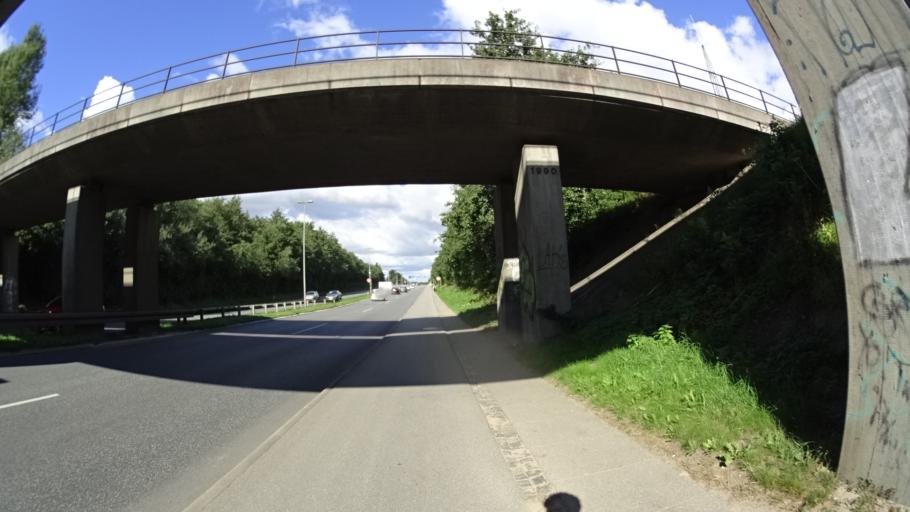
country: DK
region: Central Jutland
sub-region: Arhus Kommune
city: Stavtrup
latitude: 56.1174
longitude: 10.1490
